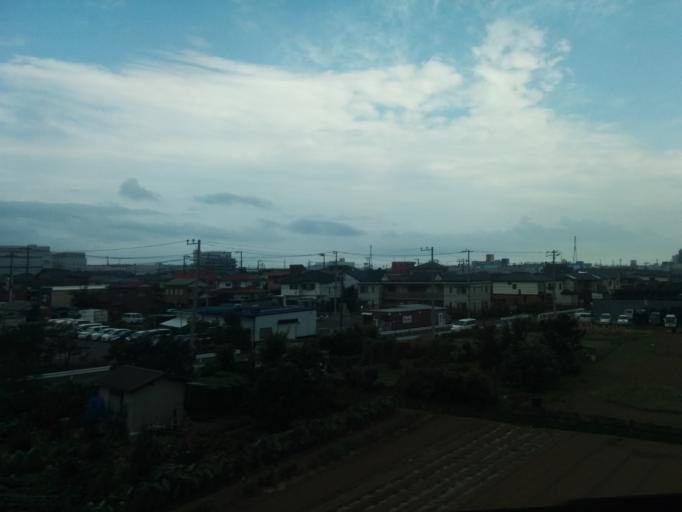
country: JP
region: Kanagawa
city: Isehara
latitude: 35.3846
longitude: 139.3607
